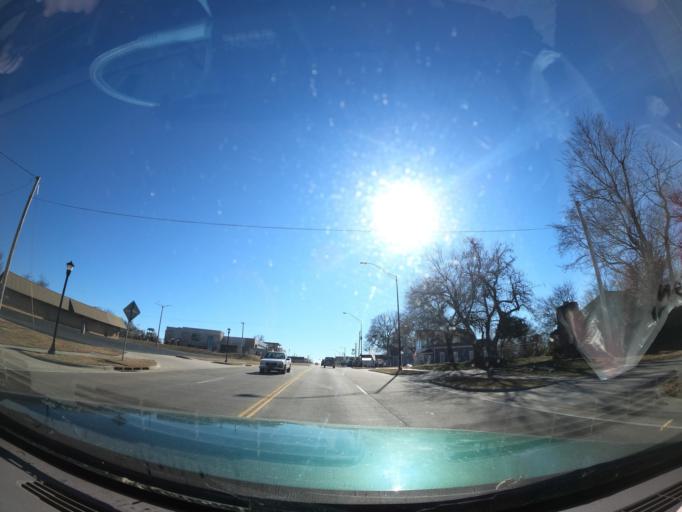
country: US
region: Oklahoma
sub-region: Wagoner County
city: Coweta
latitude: 35.9548
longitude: -95.6505
